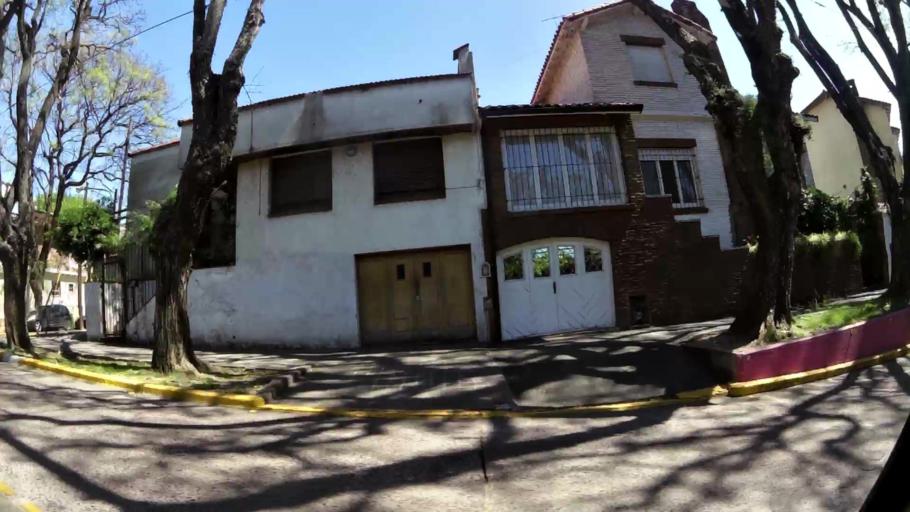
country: AR
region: Buenos Aires
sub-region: Partido de Vicente Lopez
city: Olivos
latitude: -34.5120
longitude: -58.4869
